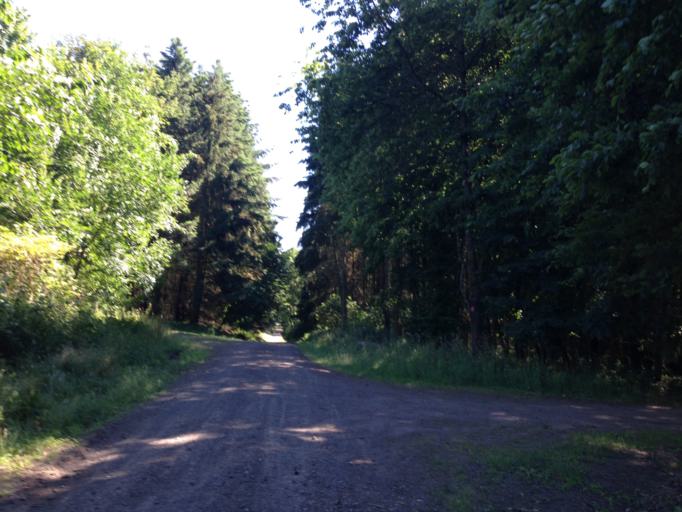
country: DE
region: Hesse
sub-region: Regierungsbezirk Giessen
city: Grossen Buseck
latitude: 50.5748
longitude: 8.7876
